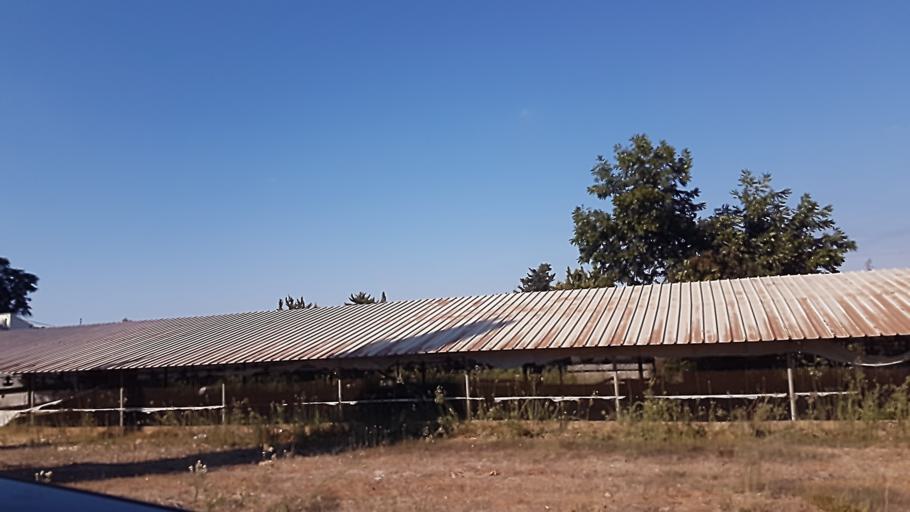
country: IL
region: Central District
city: Kfar Saba
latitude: 32.2024
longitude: 34.9093
